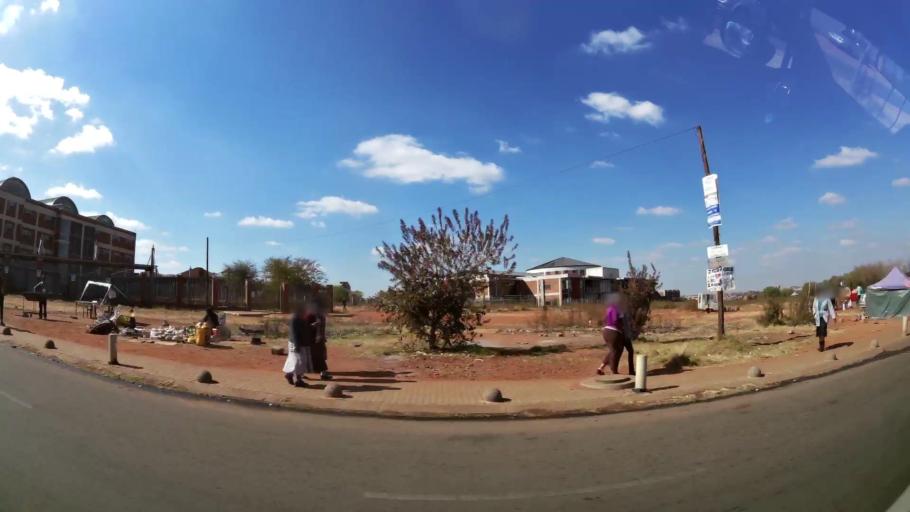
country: ZA
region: Gauteng
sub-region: West Rand District Municipality
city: Krugersdorp
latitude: -26.1646
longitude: 27.7798
